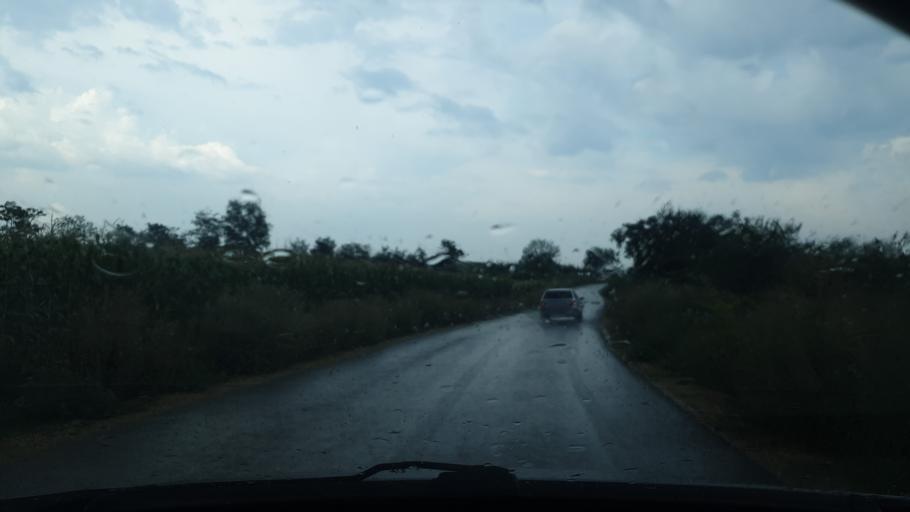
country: RS
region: Central Serbia
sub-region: Sumadijski Okrug
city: Kragujevac
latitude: 44.0764
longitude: 20.7911
